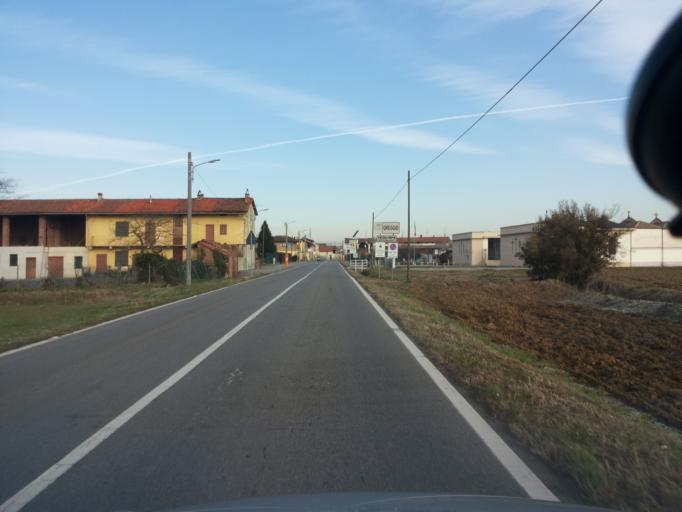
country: IT
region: Piedmont
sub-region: Provincia di Vercelli
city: Greggio
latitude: 45.4486
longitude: 8.3848
